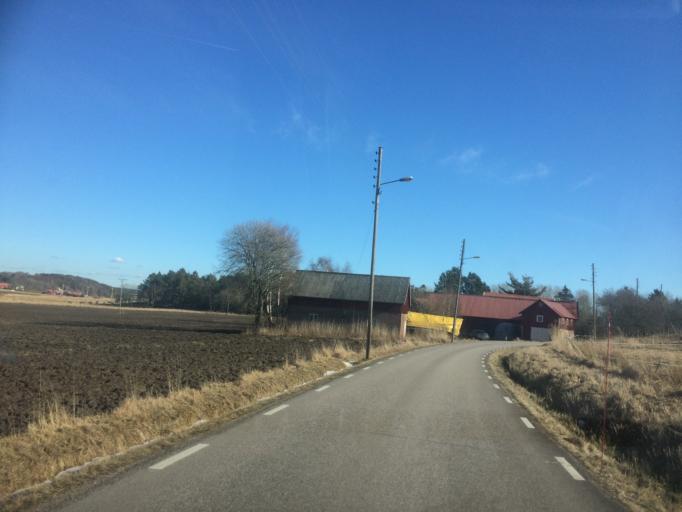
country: SE
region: Vaestra Goetaland
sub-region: Goteborg
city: Torslanda
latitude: 57.7898
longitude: 11.8593
